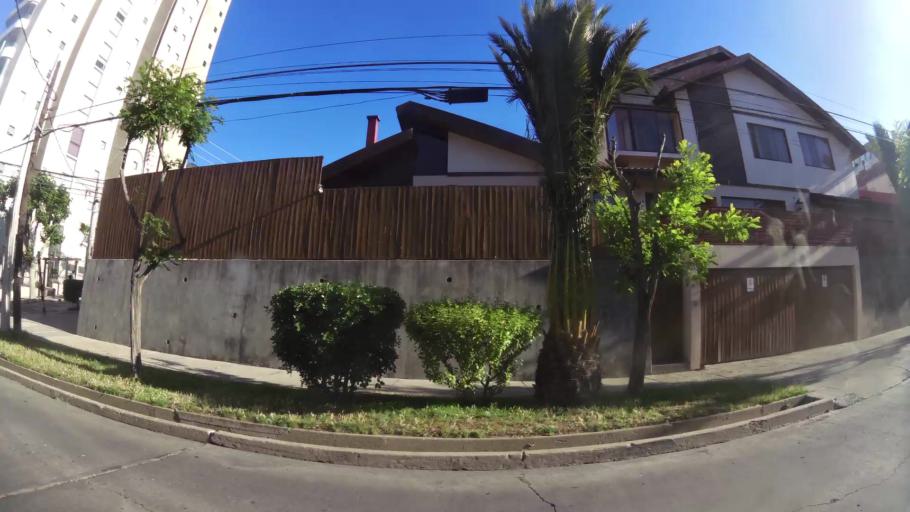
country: CL
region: Valparaiso
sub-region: Provincia de Valparaiso
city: Vina del Mar
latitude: -33.0279
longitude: -71.5820
